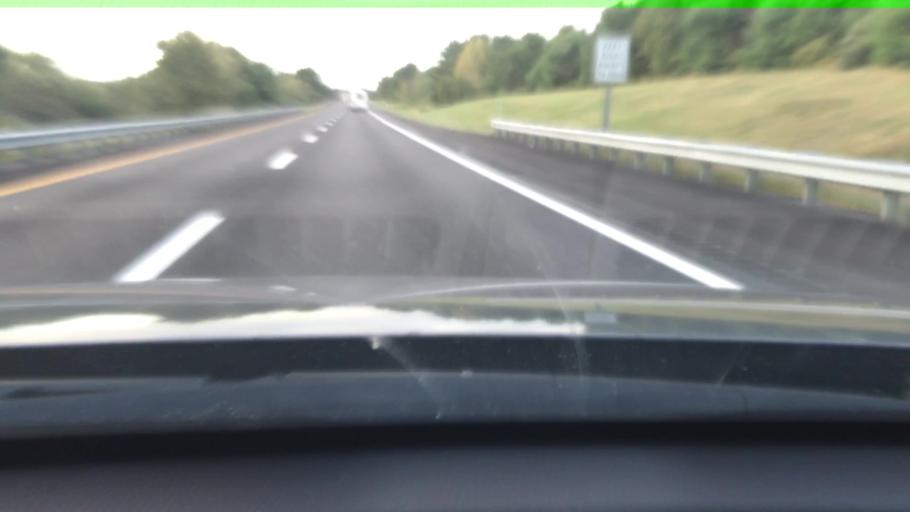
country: US
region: Maine
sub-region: Sagadahoc County
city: Richmond
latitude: 44.0736
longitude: -69.8799
